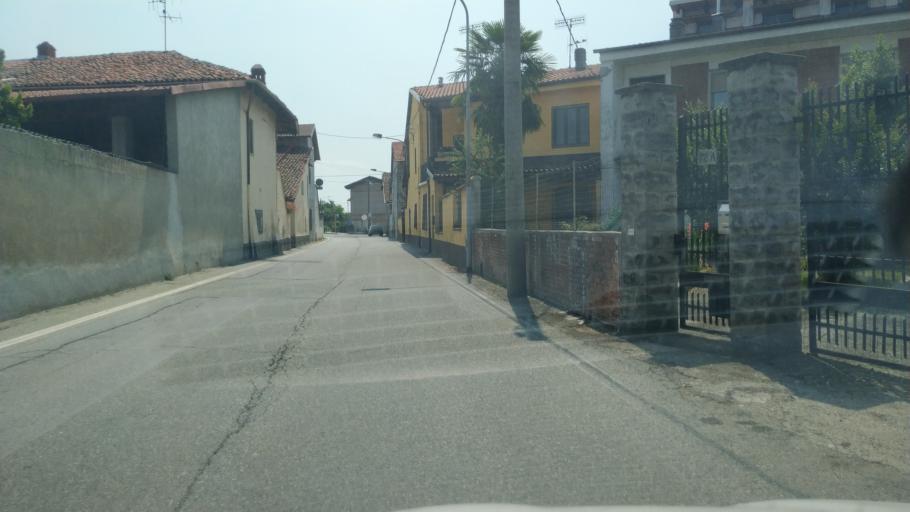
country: IT
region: Piedmont
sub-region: Provincia di Torino
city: Rondissone
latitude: 45.2445
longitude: 7.9678
